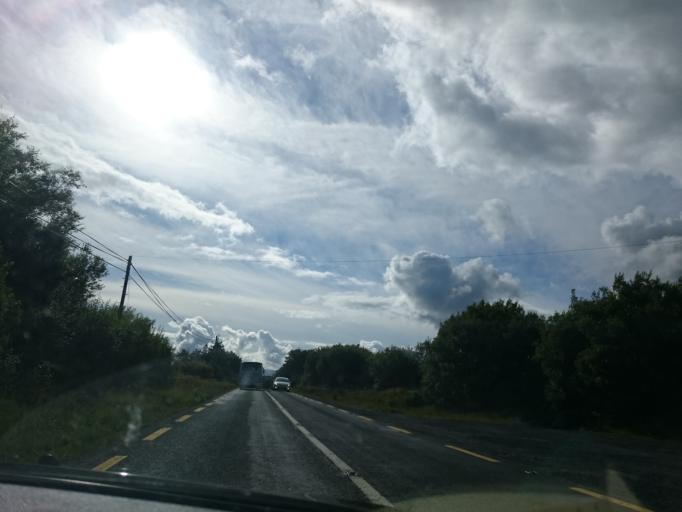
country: IE
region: Connaught
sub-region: Maigh Eo
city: Westport
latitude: 53.9014
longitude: -9.6091
